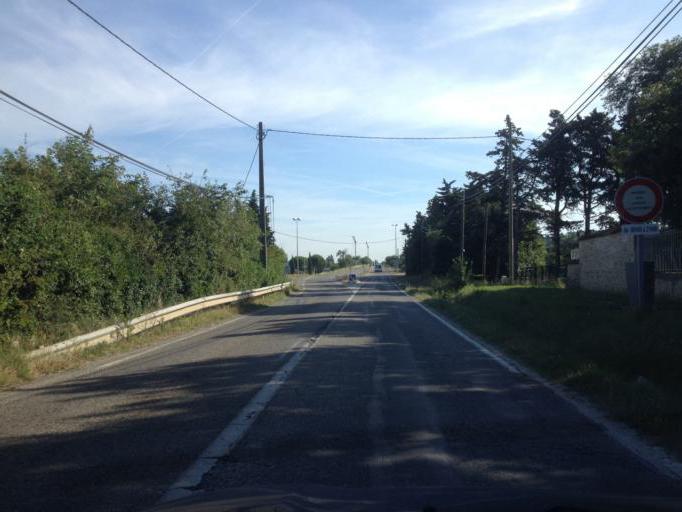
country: FR
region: Provence-Alpes-Cote d'Azur
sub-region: Departement du Vaucluse
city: Orange
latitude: 44.1193
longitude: 4.7975
